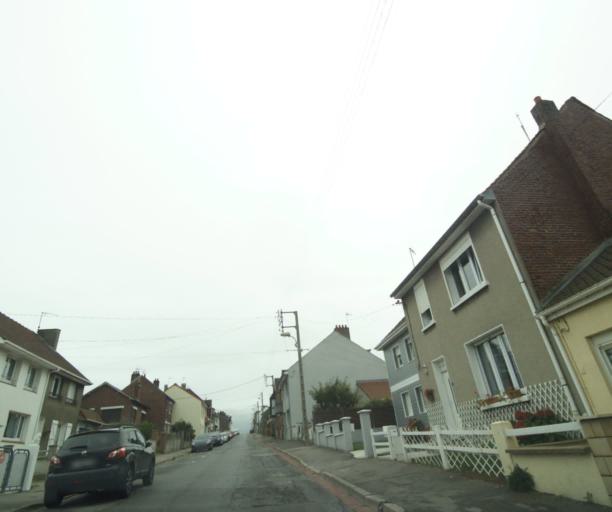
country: FR
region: Nord-Pas-de-Calais
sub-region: Departement du Pas-de-Calais
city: Etaples
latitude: 50.5200
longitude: 1.6335
